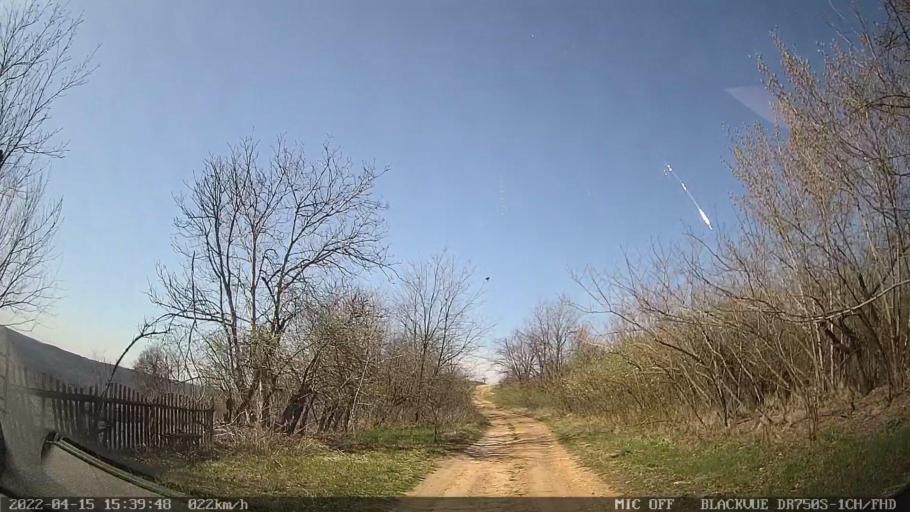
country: MD
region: Raionul Ocnita
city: Otaci
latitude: 48.3542
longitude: 27.9267
